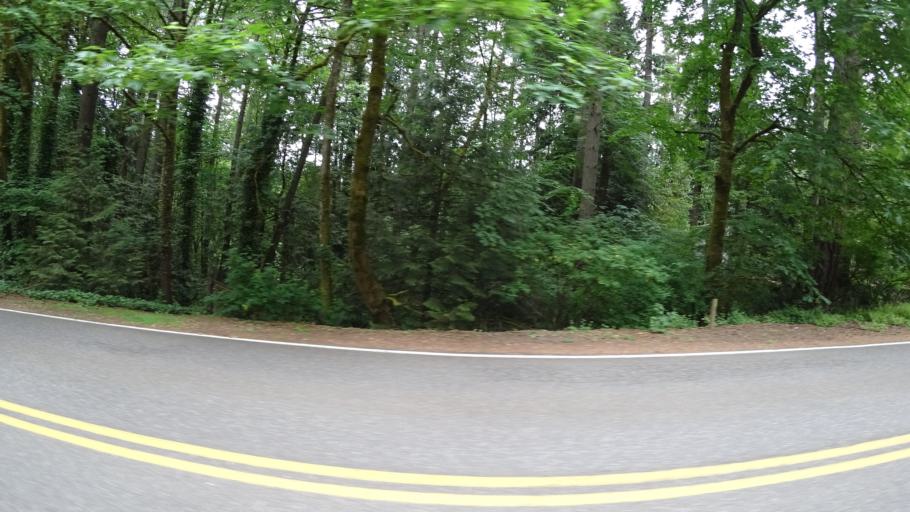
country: US
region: Oregon
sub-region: Clackamas County
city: Lake Oswego
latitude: 45.4458
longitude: -122.7050
